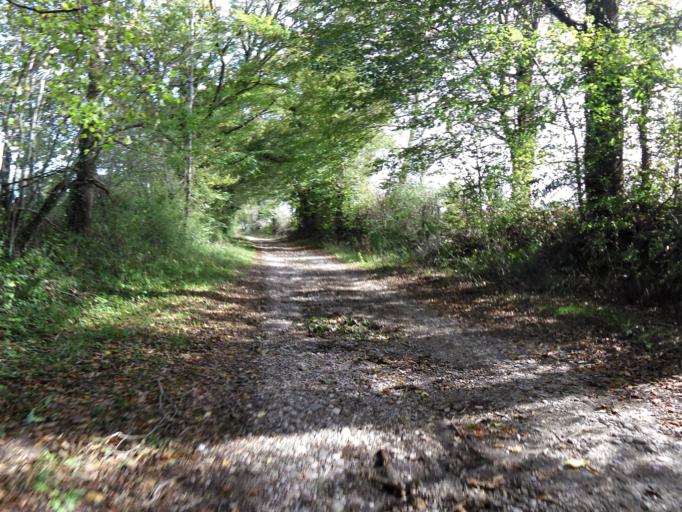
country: FR
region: Rhone-Alpes
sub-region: Departement de l'Ain
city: Perouges
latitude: 45.9118
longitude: 5.1556
